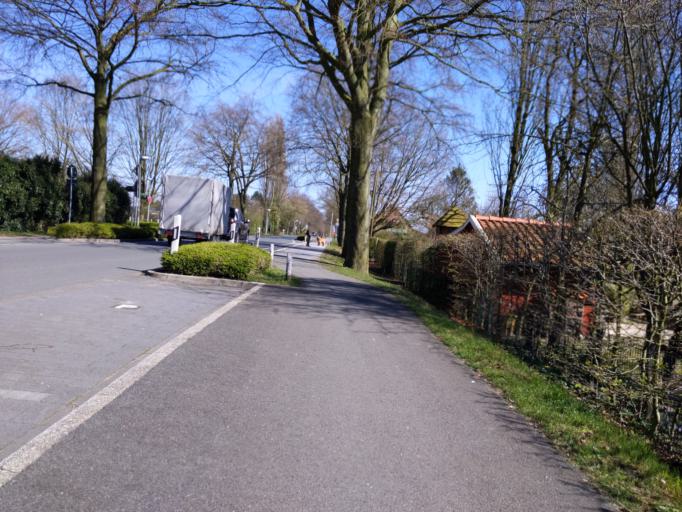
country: DE
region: North Rhine-Westphalia
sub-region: Regierungsbezirk Dusseldorf
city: Schermbeck
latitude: 51.6959
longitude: 6.8843
